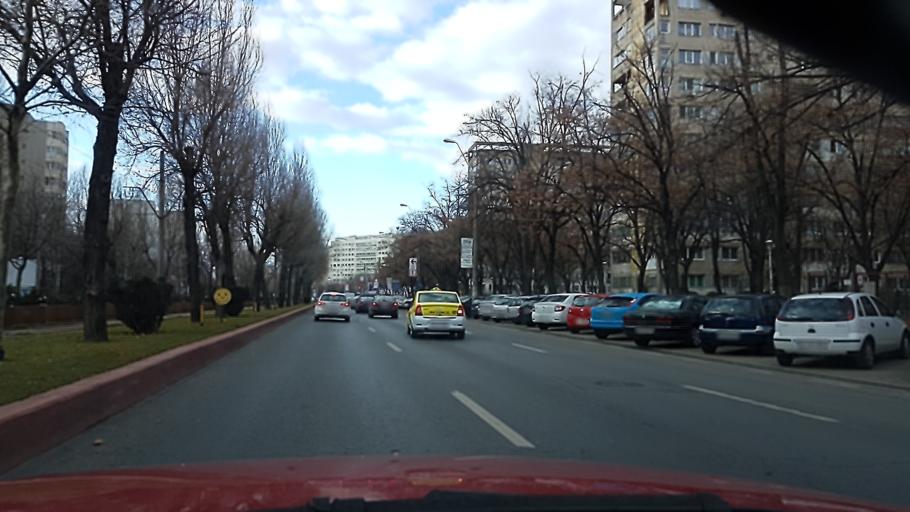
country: RO
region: Ilfov
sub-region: Comuna Popesti-Leordeni
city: Popesti-Leordeni
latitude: 44.4168
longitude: 26.1486
